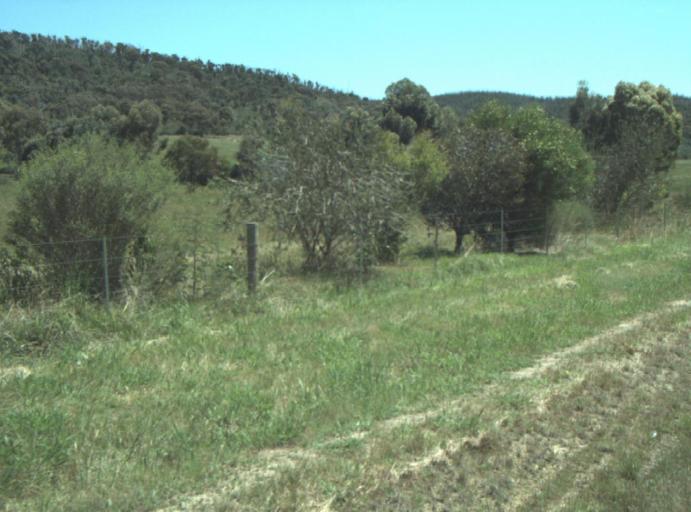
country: AU
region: Victoria
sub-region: Greater Geelong
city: Lara
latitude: -37.8496
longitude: 144.2817
